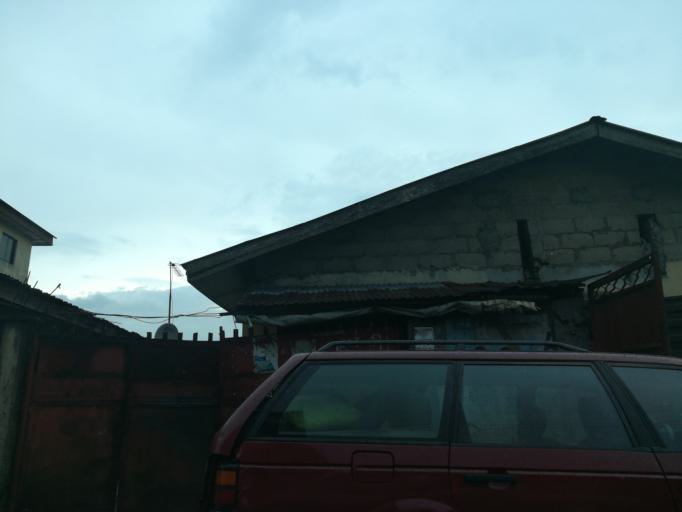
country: NG
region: Rivers
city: Port Harcourt
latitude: 4.7950
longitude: 6.9917
